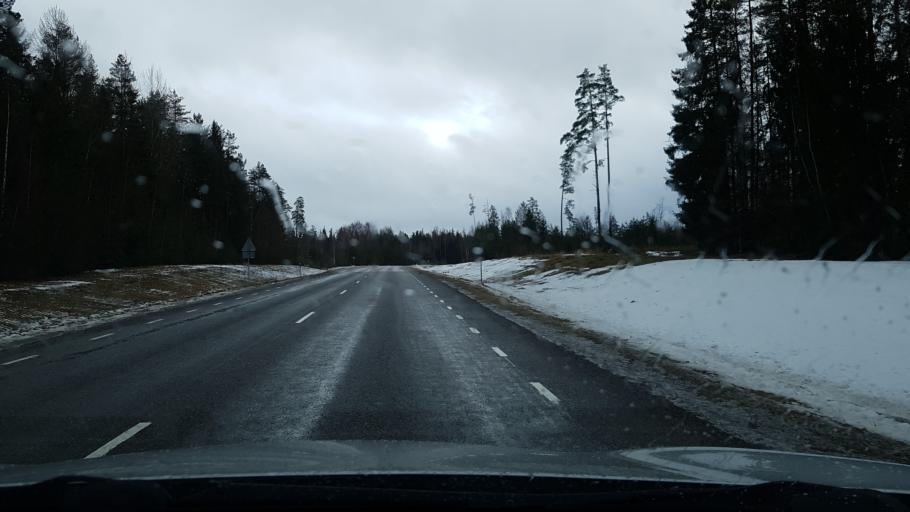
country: LV
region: Apes Novads
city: Ape
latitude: 57.6262
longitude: 26.6374
